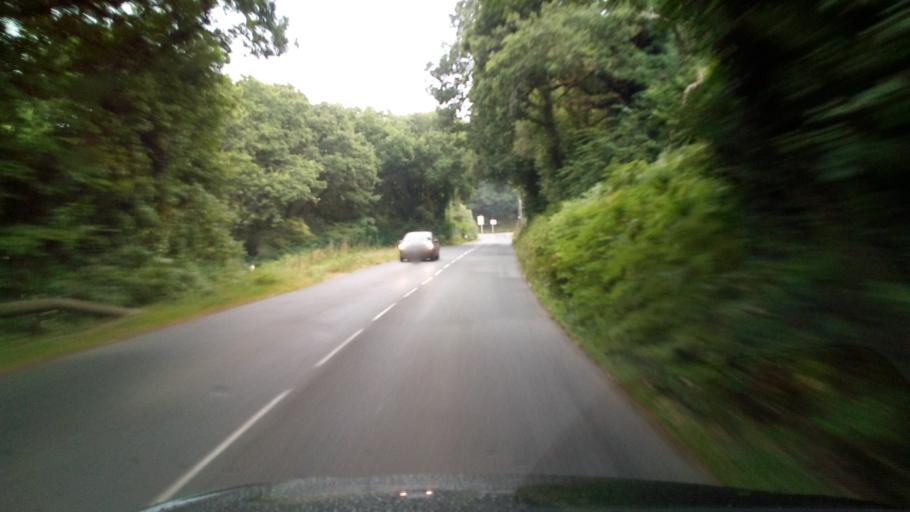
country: FR
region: Brittany
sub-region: Departement du Finistere
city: Landivisiau
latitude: 48.4973
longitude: -4.0882
